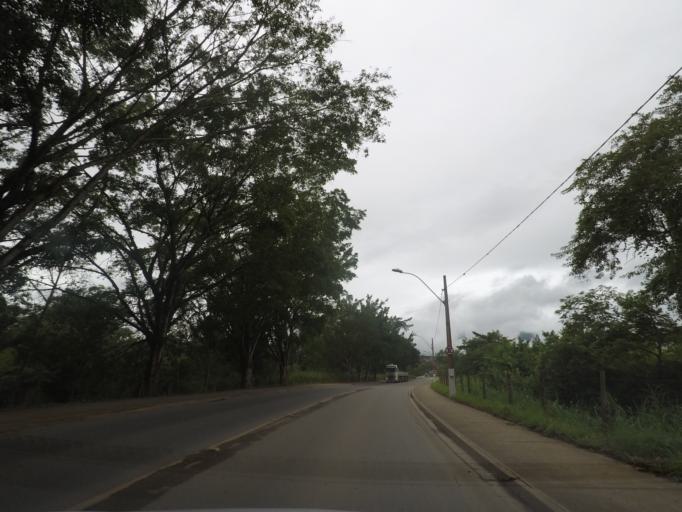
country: BR
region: Sao Paulo
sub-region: Cajati
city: Cajati
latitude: -24.7258
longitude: -48.0983
